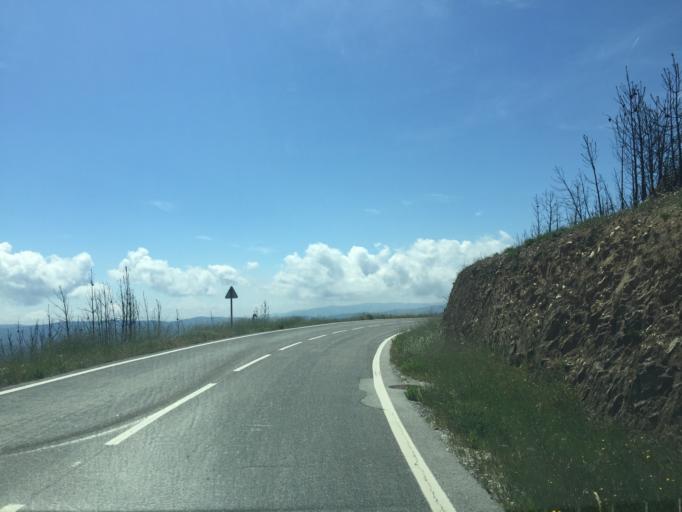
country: PT
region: Coimbra
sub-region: Pampilhosa da Serra
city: Pampilhosa da Serra
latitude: 40.0219
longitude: -7.9643
